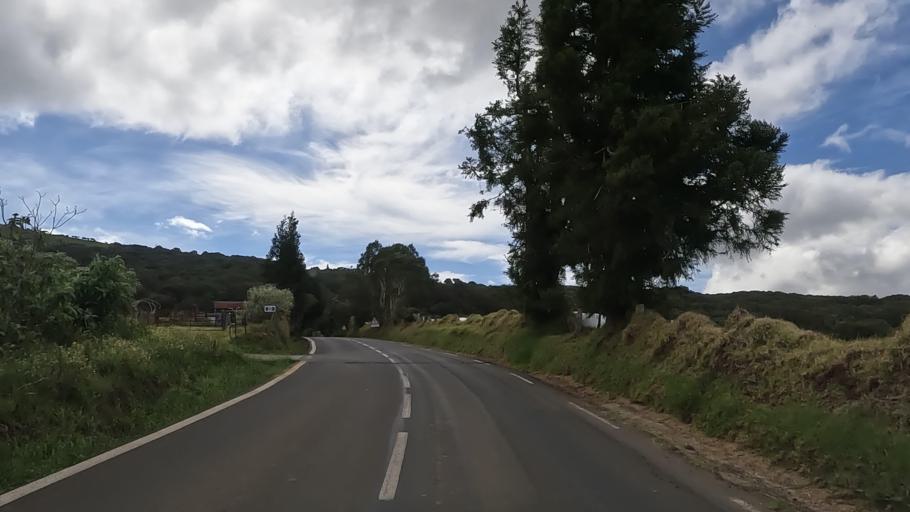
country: RE
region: Reunion
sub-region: Reunion
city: Le Tampon
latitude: -21.2377
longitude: 55.5827
